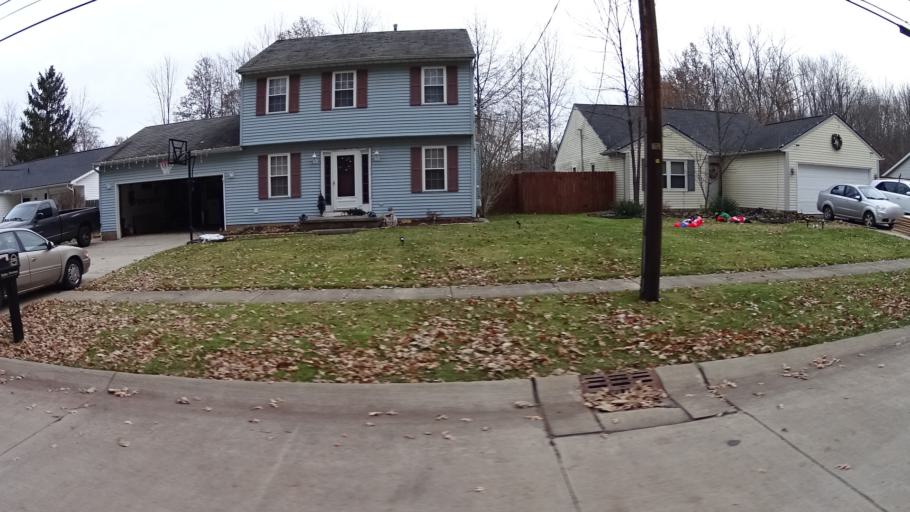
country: US
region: Ohio
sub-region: Lorain County
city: North Ridgeville
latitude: 41.3868
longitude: -82.0638
